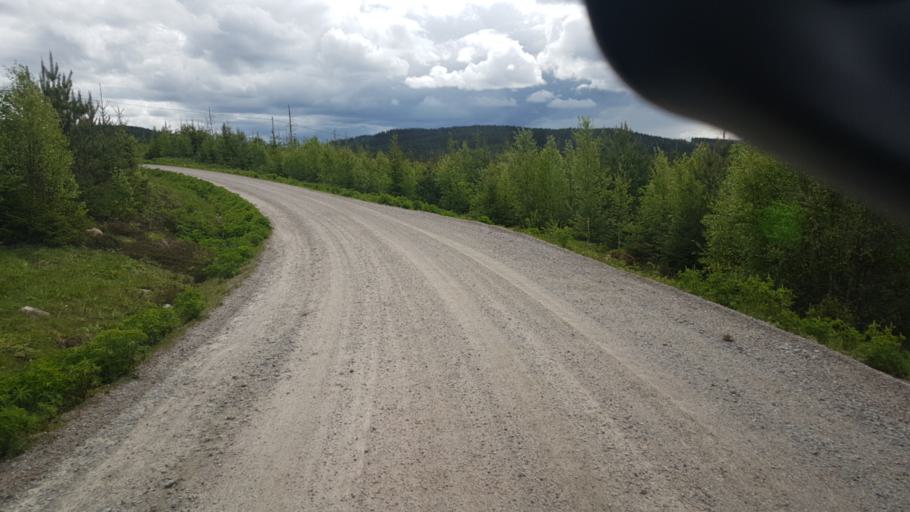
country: SE
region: Vaermland
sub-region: Arvika Kommun
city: Arvika
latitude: 59.8296
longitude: 12.8289
